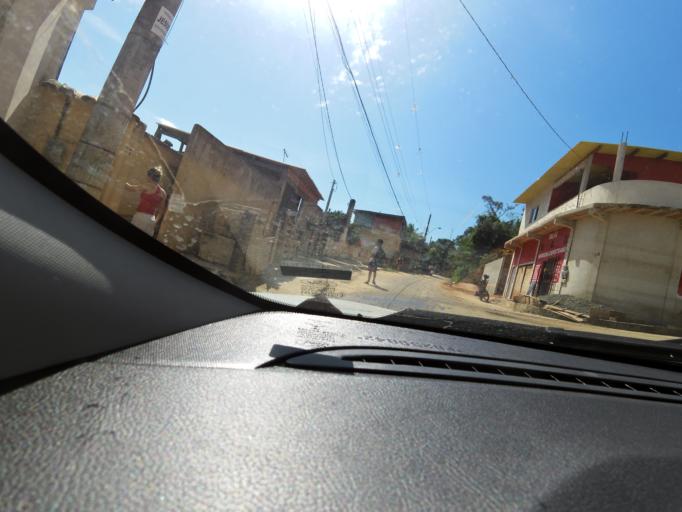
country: BR
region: Espirito Santo
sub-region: Guarapari
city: Guarapari
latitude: -20.6579
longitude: -40.5214
